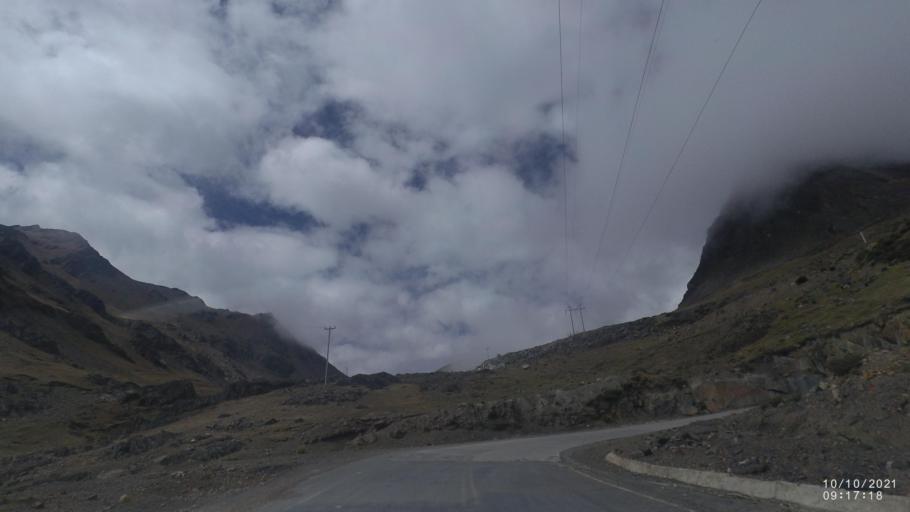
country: BO
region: La Paz
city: Quime
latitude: -17.0489
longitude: -67.2962
